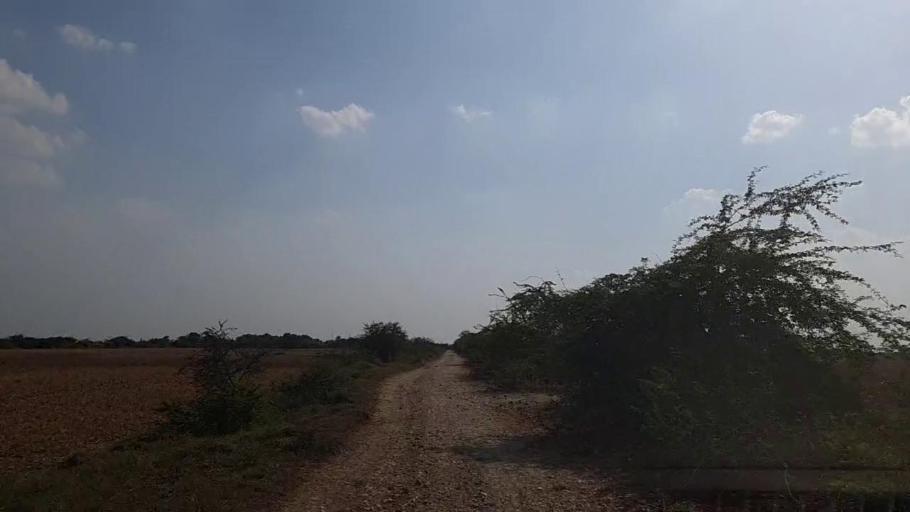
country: PK
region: Sindh
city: Jati
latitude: 24.4815
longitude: 68.3403
